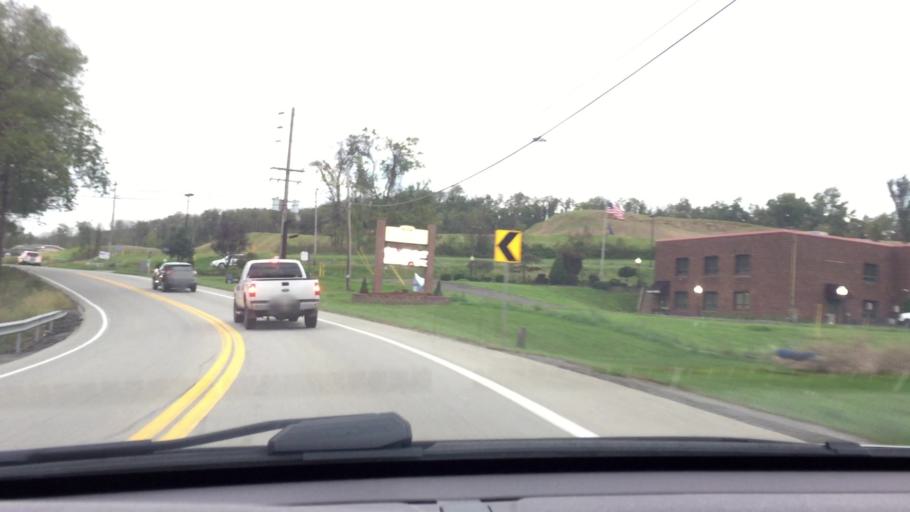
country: US
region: Pennsylvania
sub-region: Washington County
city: Canonsburg
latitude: 40.2354
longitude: -80.1693
